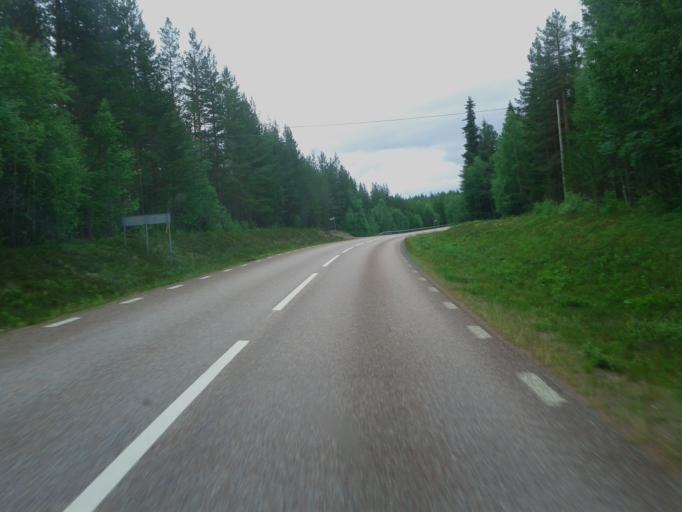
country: NO
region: Hedmark
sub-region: Trysil
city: Innbygda
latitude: 61.7225
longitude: 12.9976
